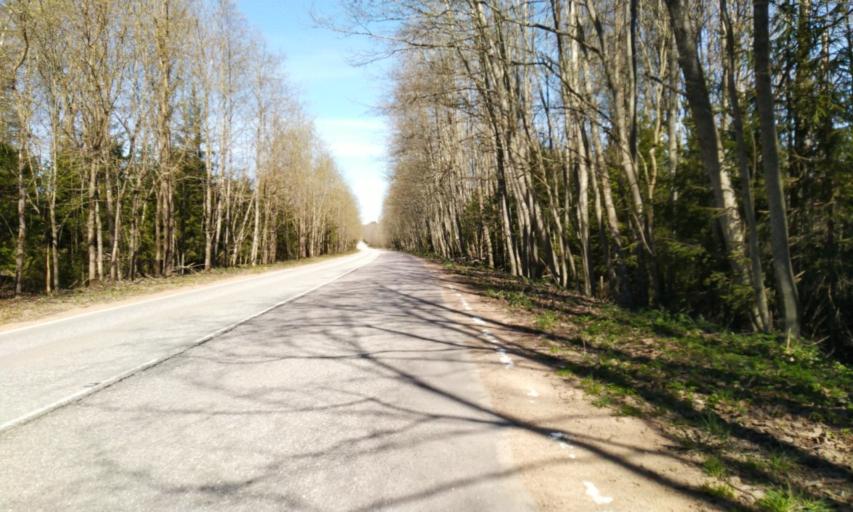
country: RU
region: Leningrad
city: Garbolovo
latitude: 60.4028
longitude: 30.4732
